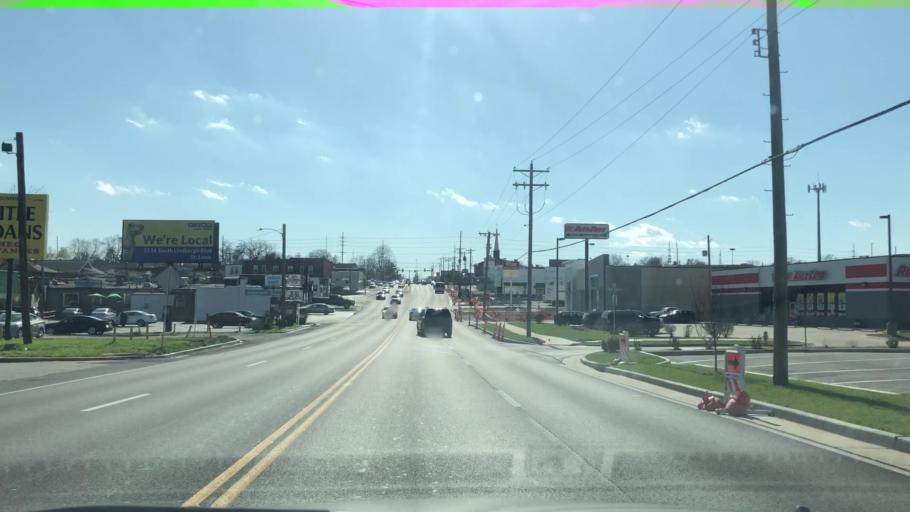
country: US
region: Missouri
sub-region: Saint Louis County
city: Affton
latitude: 38.5537
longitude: -90.3198
